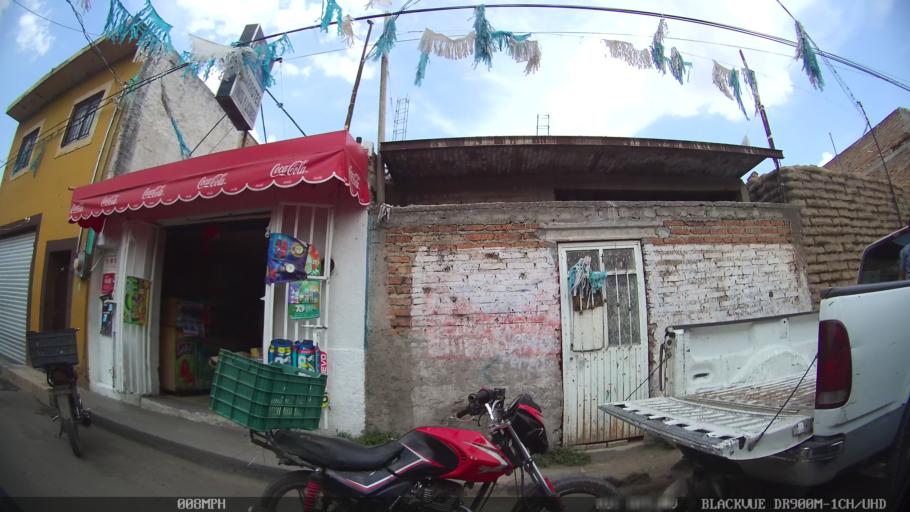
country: MX
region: Jalisco
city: Tonala
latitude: 20.6772
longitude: -103.2444
